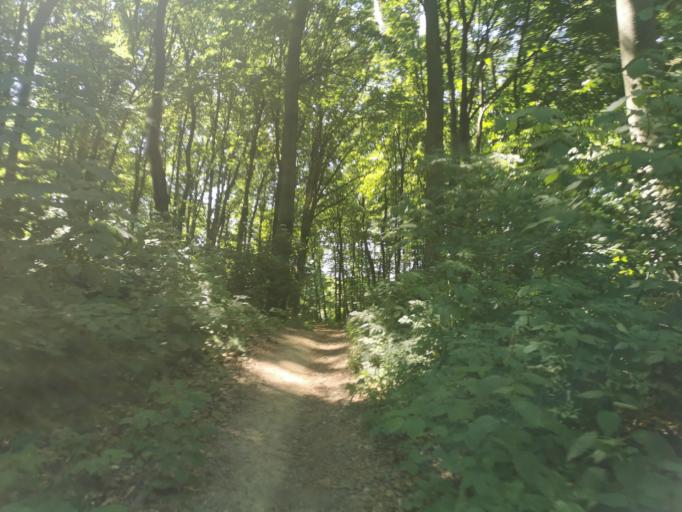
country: SK
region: Trnavsky
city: Smolenice
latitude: 48.5577
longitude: 17.4384
